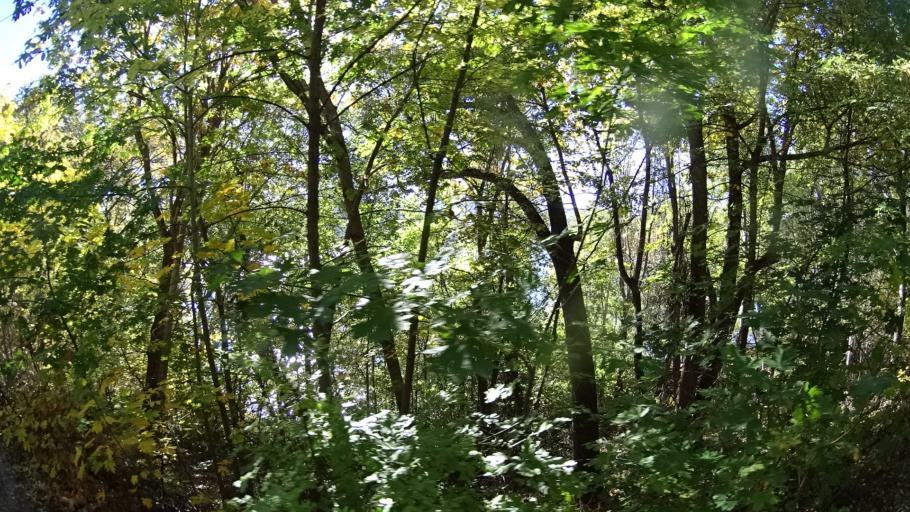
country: US
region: California
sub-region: Siskiyou County
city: Montague
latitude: 41.9879
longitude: -122.3258
